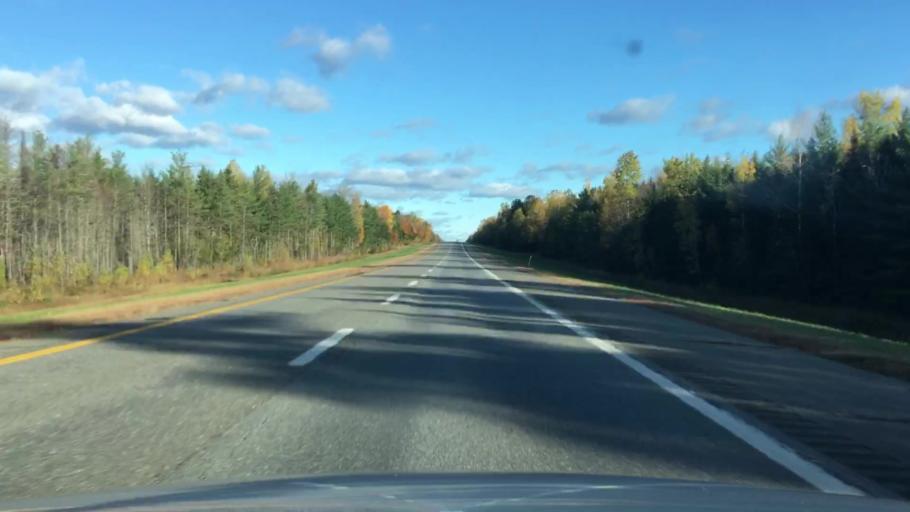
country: US
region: Maine
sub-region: Penobscot County
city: Greenbush
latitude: 45.0641
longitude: -68.6890
